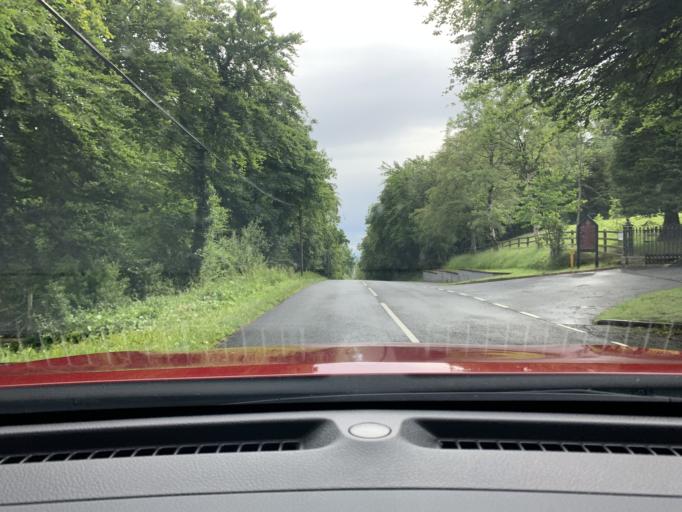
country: GB
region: Northern Ireland
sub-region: Fermanagh District
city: Enniskillen
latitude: 54.2583
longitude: -7.7554
